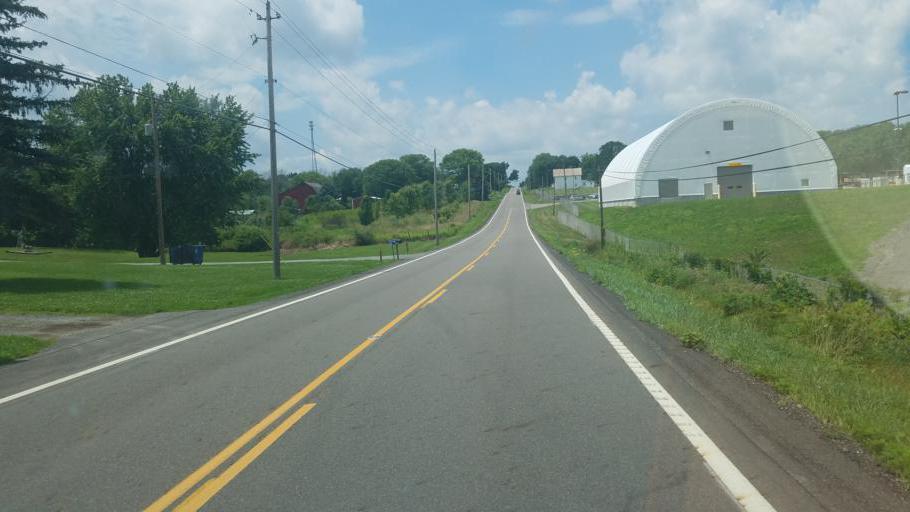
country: US
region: Ohio
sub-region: Columbiana County
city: Lisbon
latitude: 40.7690
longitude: -80.8088
